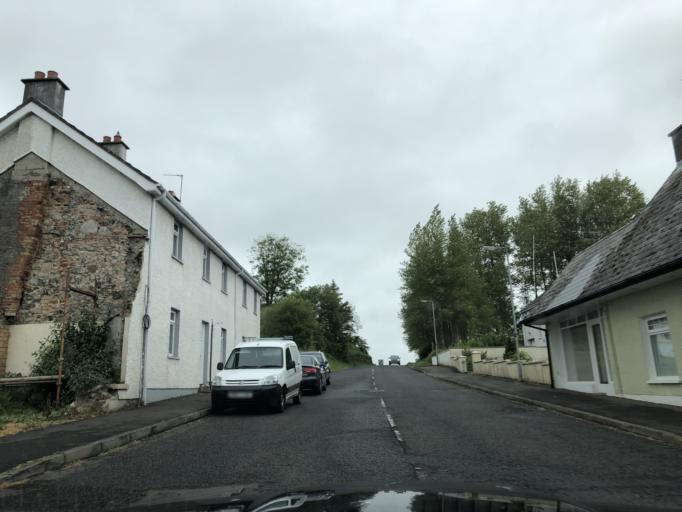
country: GB
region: Northern Ireland
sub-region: Ballymoney District
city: Ballymoney
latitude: 55.1249
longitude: -6.4684
